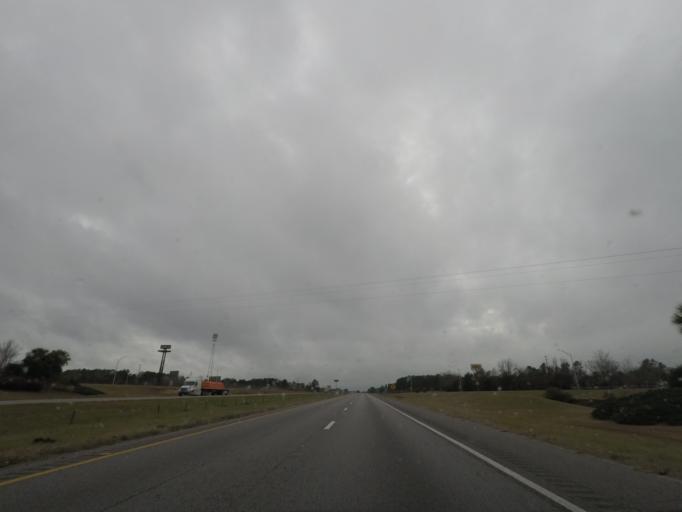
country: US
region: South Carolina
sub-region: Orangeburg County
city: Holly Hill
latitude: 33.4853
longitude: -80.4716
